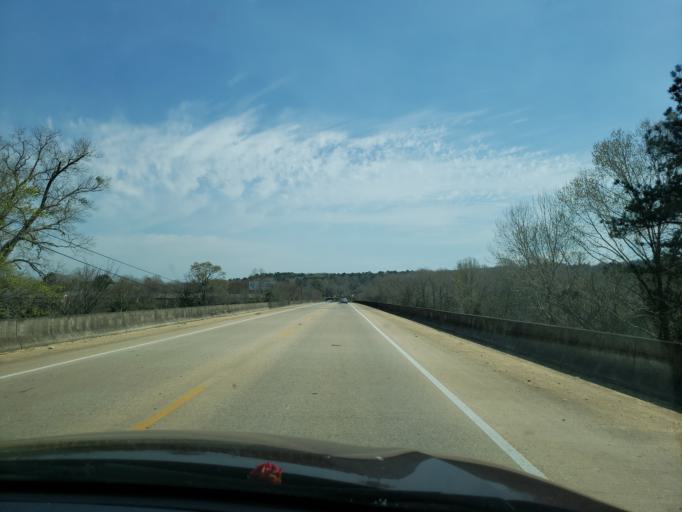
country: US
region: Alabama
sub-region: Elmore County
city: Wetumpka
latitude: 32.5508
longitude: -86.1966
